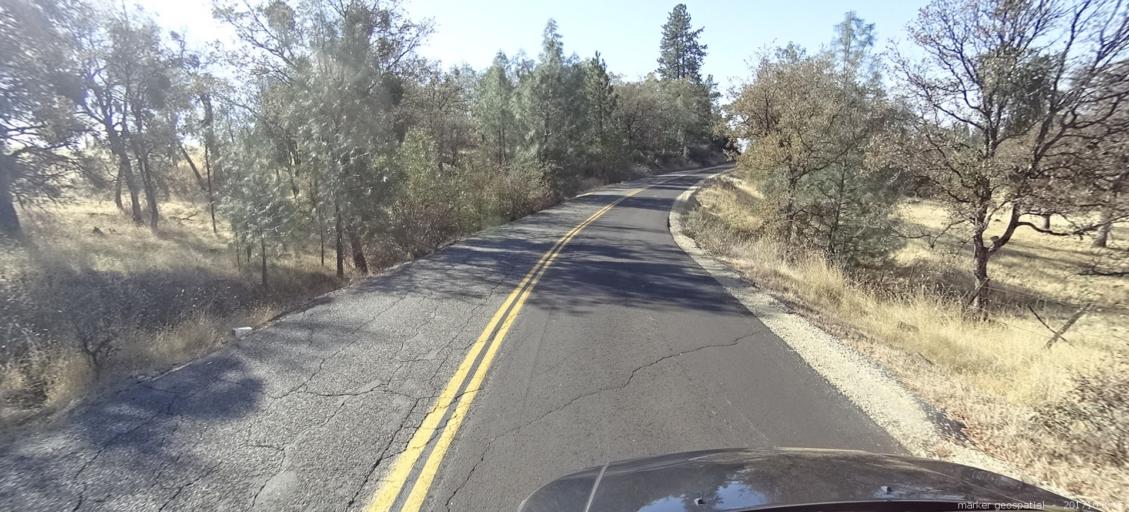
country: US
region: California
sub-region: Shasta County
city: Shingletown
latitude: 40.6665
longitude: -121.9461
